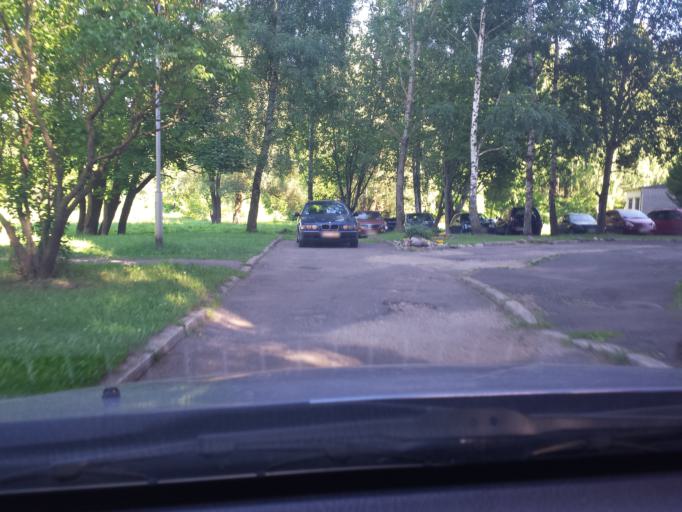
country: LV
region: Riga
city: Jaunciems
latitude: 56.9941
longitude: 24.1944
